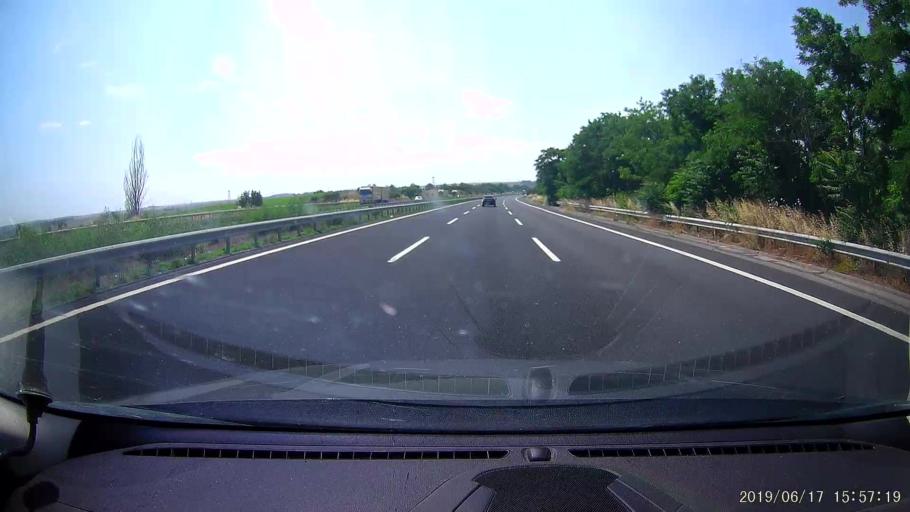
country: TR
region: Tekirdag
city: Cerkezkoey
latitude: 41.2110
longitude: 27.9595
